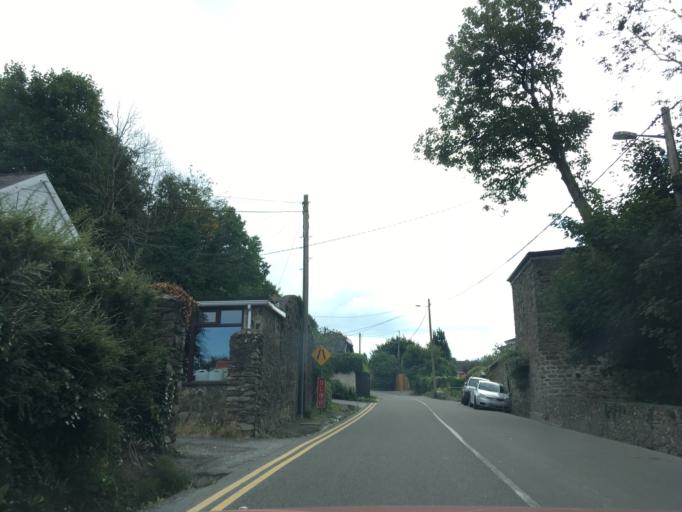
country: IE
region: Munster
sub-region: County Cork
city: Crosshaven
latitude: 51.8012
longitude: -8.2943
